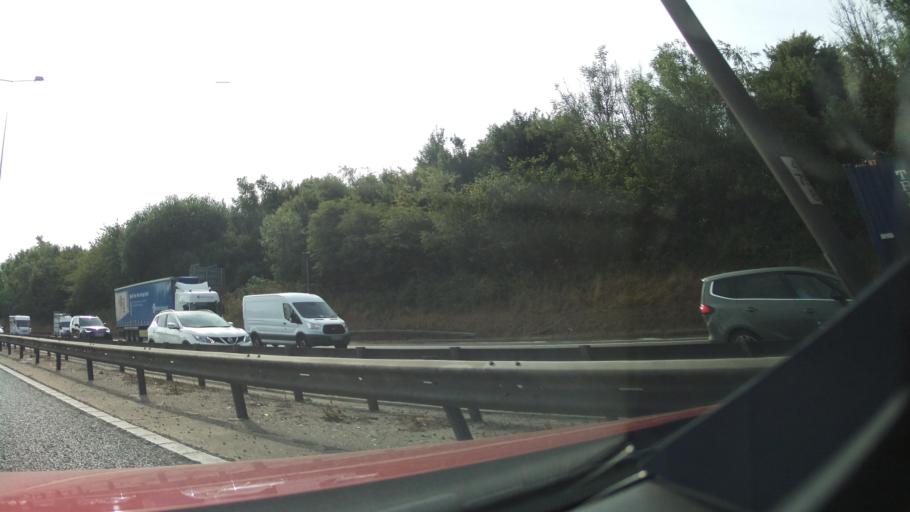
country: GB
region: England
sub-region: Surrey
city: Reigate
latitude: 51.2580
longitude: -0.2136
